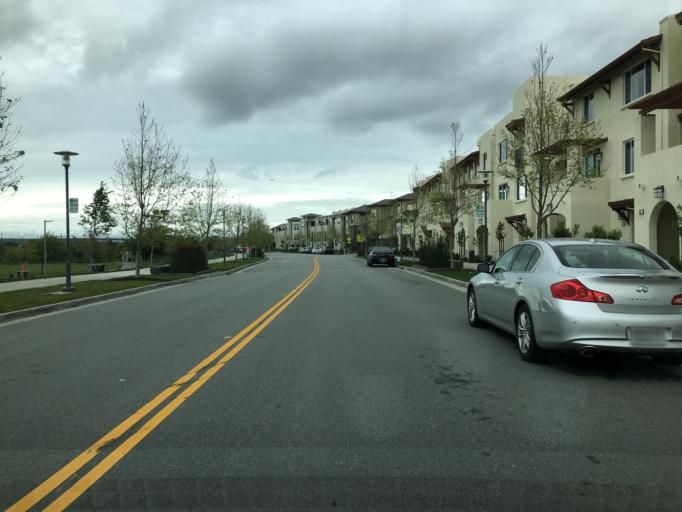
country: US
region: California
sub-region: San Mateo County
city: Foster City
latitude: 37.5443
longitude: -122.2985
